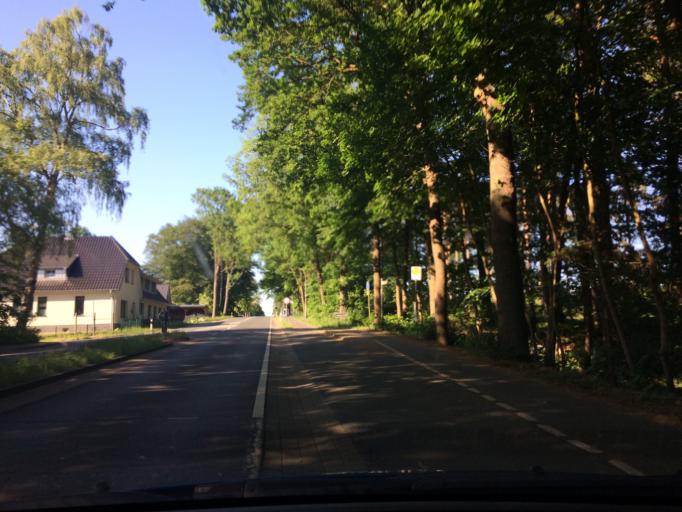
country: DE
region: Lower Saxony
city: Soltau
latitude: 53.0020
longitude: 9.8395
